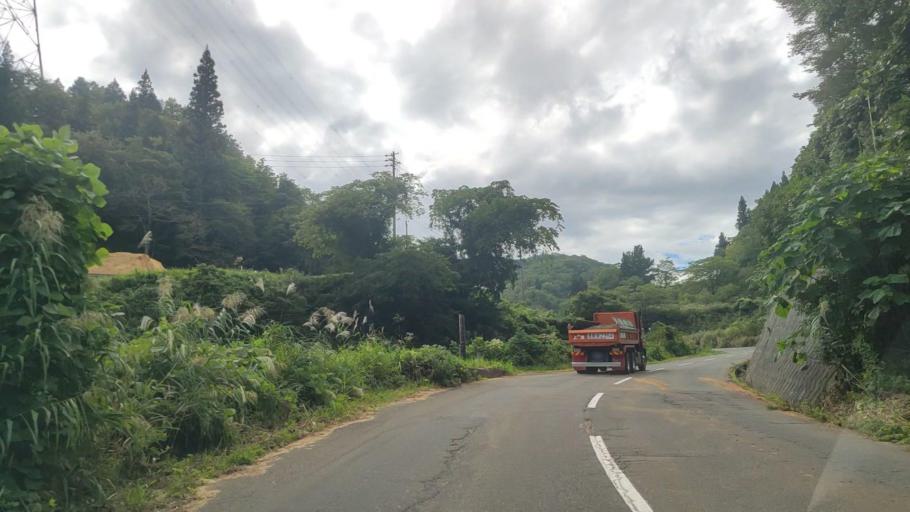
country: JP
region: Nagano
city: Iiyama
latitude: 36.8895
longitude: 138.3231
